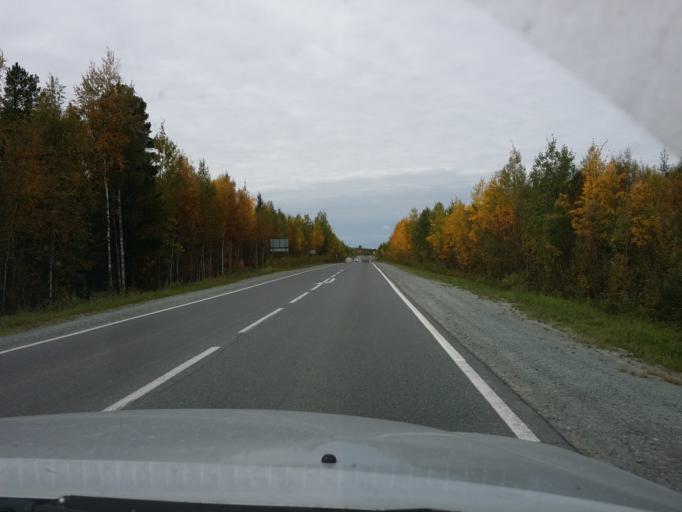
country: RU
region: Khanty-Mansiyskiy Avtonomnyy Okrug
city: Megion
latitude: 61.1057
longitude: 75.8976
